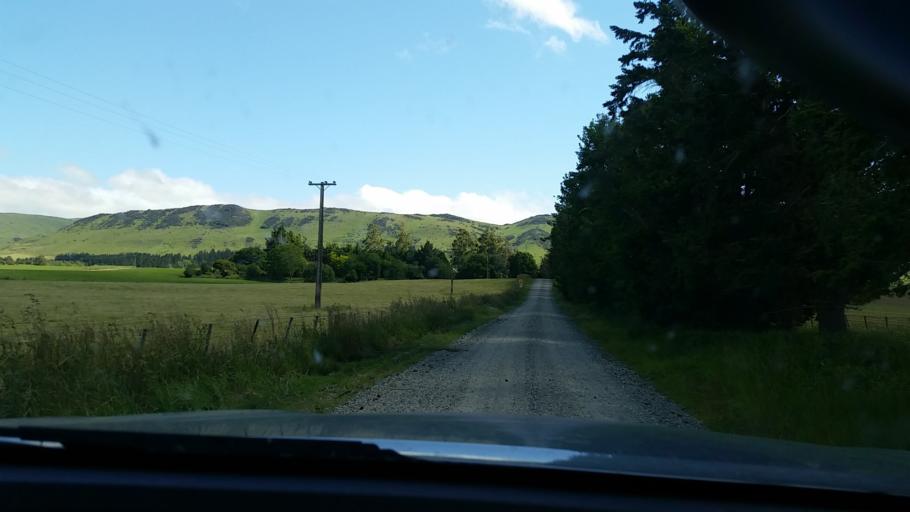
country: NZ
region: Southland
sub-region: Southland District
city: Winton
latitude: -45.9030
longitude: 168.5528
